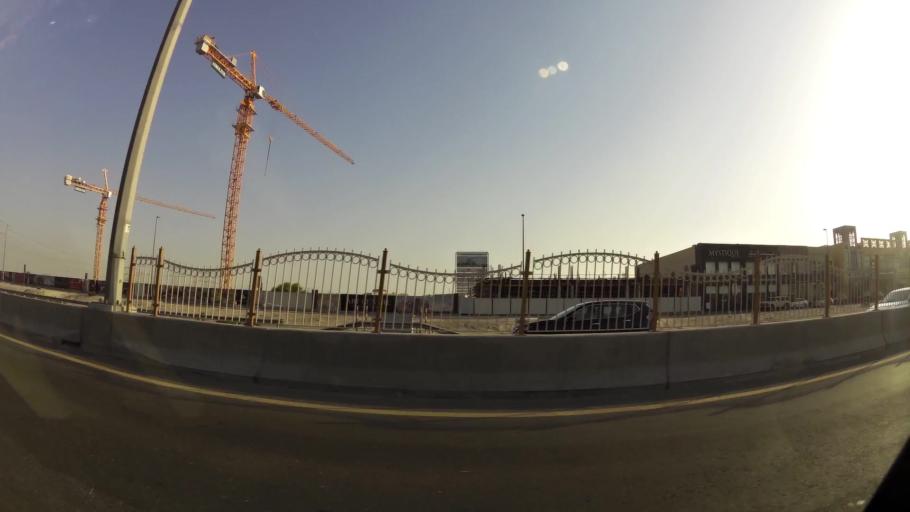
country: AE
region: Dubai
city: Dubai
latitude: 25.1061
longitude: 55.2276
